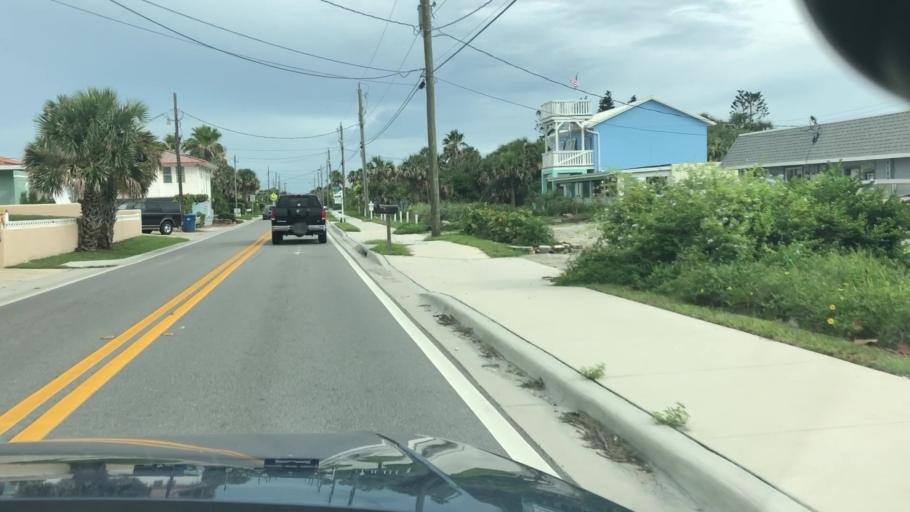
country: US
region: Florida
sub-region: Volusia County
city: Ponce Inlet
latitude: 29.1297
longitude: -80.9568
